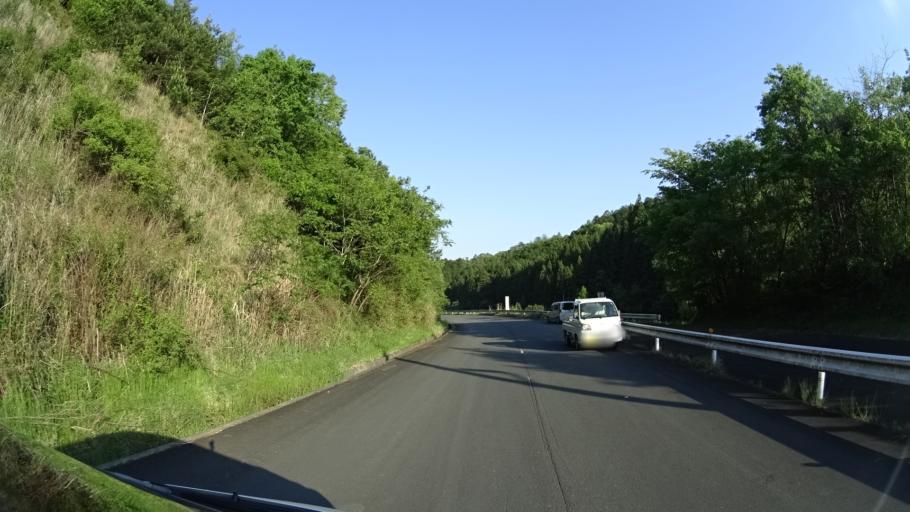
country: JP
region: Kyoto
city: Kameoka
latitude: 35.1108
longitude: 135.4367
